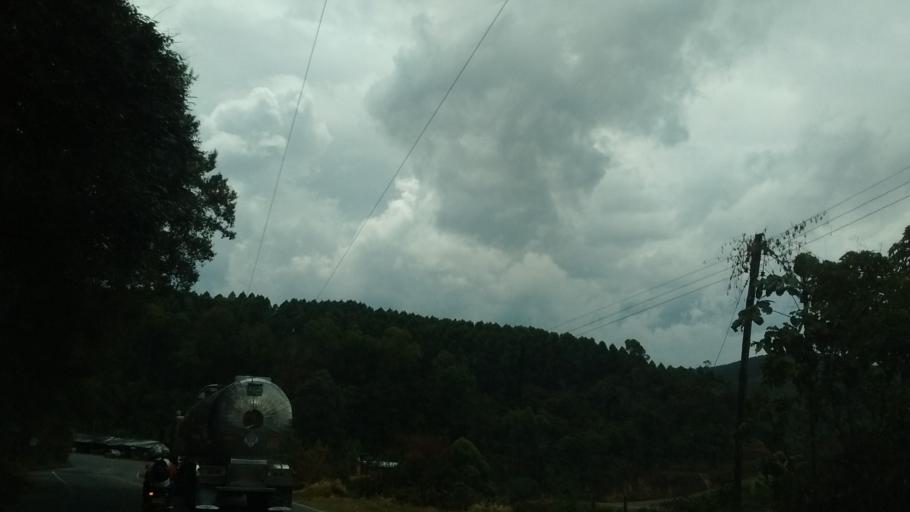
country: CO
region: Cauca
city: Rosas
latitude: 2.3084
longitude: -76.6859
